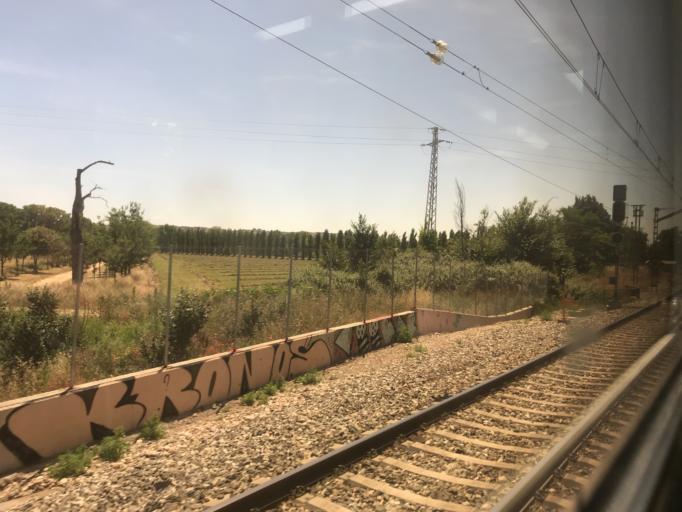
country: ES
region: Madrid
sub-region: Provincia de Madrid
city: Aranjuez
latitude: 40.0427
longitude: -3.6211
